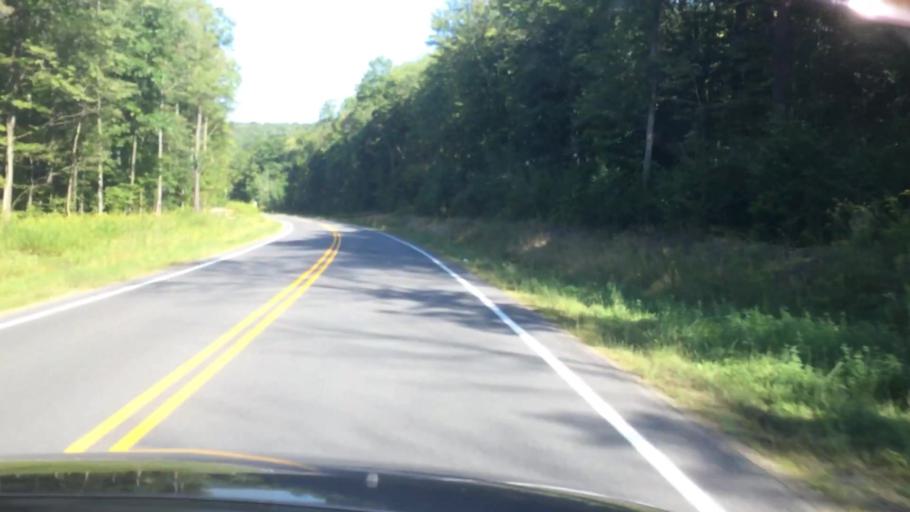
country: US
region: Pennsylvania
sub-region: McKean County
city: Bradford
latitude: 41.8819
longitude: -78.5778
